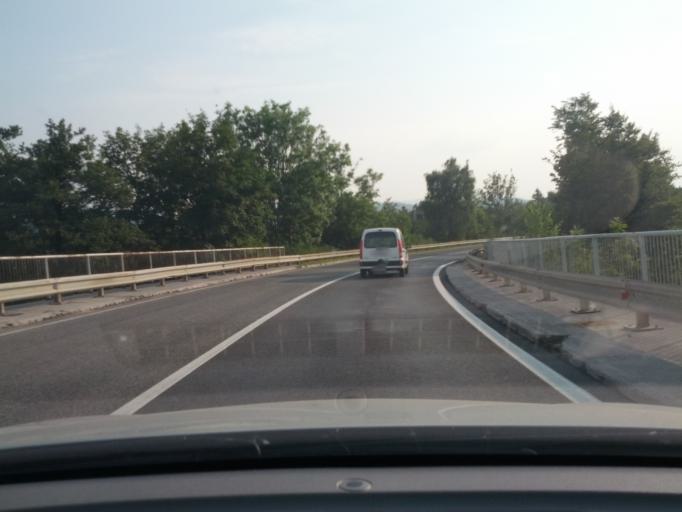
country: SI
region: Brezovica
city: Vnanje Gorice
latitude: 46.0251
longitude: 14.4336
